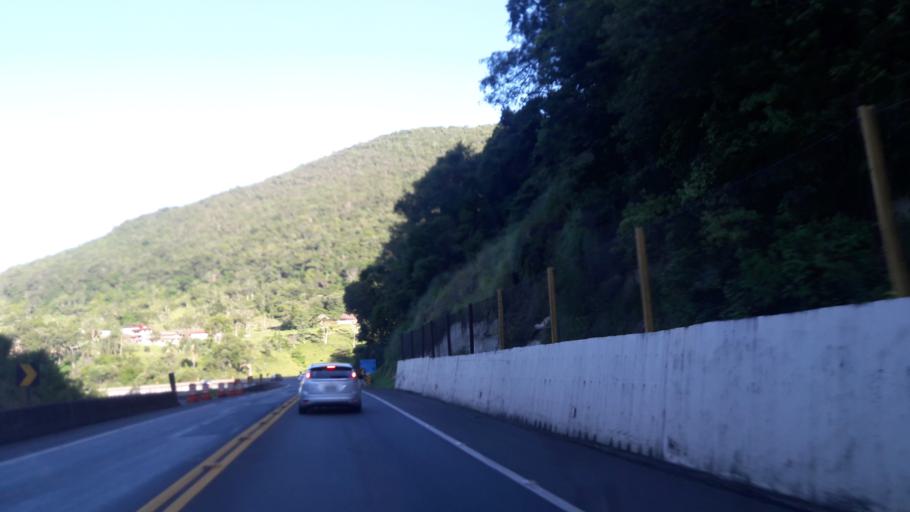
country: BR
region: Parana
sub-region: Prudentopolis
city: Prudentopolis
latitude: -25.3242
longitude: -51.1944
